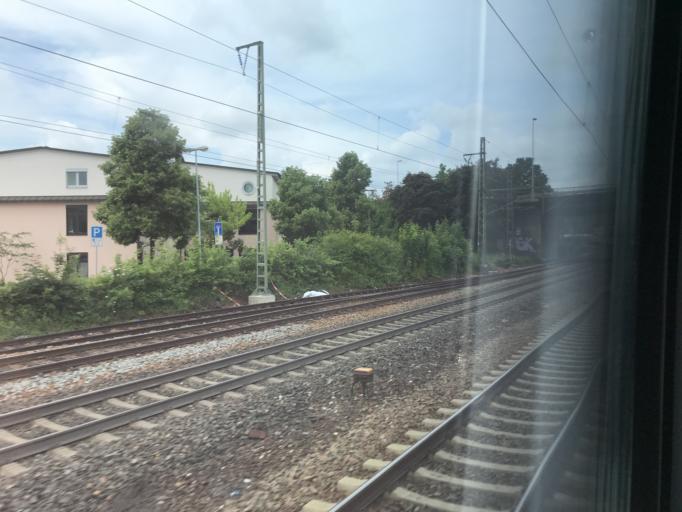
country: DE
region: Baden-Wuerttemberg
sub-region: Regierungsbezirk Stuttgart
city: Sussen
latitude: 48.6812
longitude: 9.7643
